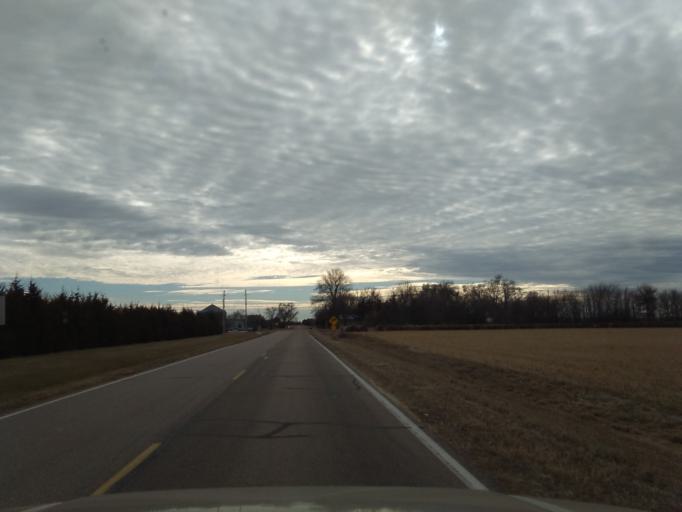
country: US
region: Nebraska
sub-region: Buffalo County
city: Gibbon
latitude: 40.6492
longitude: -98.8473
